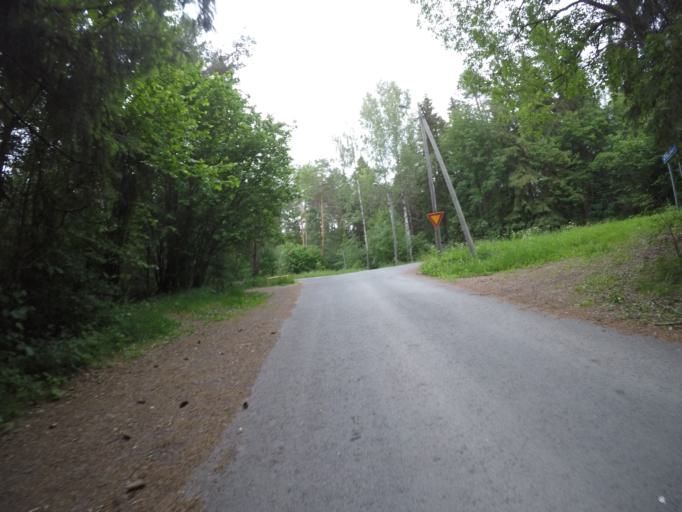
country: FI
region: Haeme
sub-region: Haemeenlinna
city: Haemeenlinna
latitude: 60.9778
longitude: 24.4529
